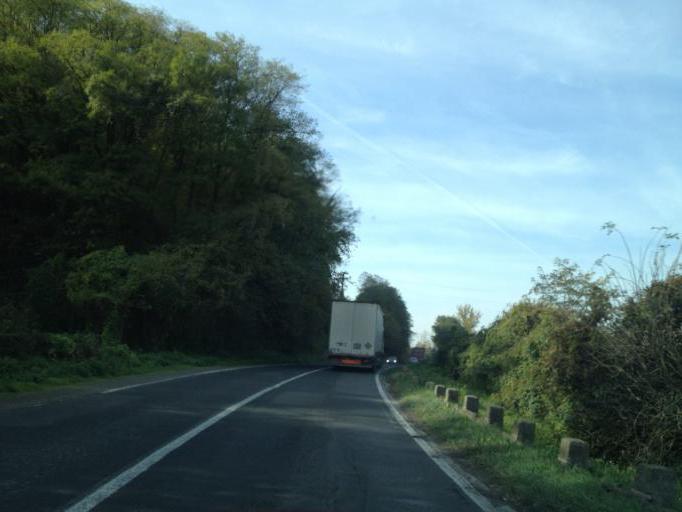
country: RO
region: Hunedoara
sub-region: Comuna Ilia
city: Ilia
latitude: 45.9179
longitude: 22.6396
